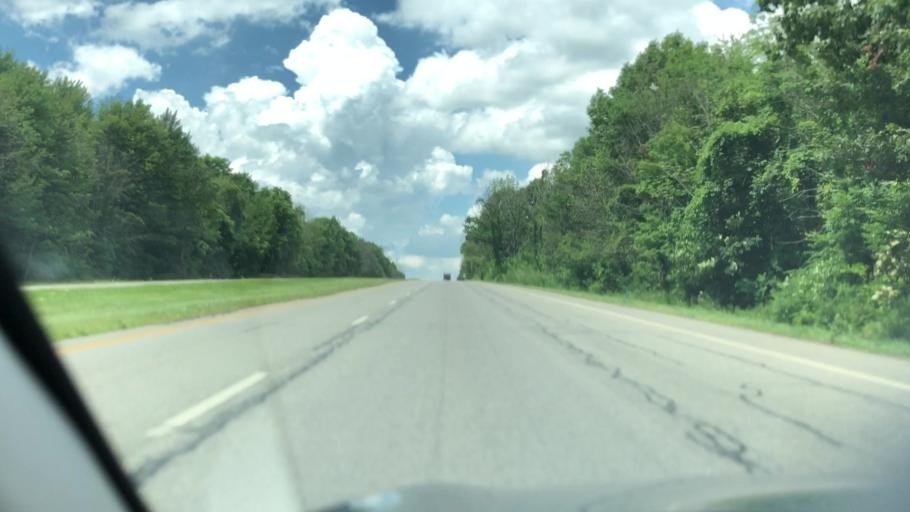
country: US
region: Ohio
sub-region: Stark County
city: Canal Fulton
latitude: 40.8802
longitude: -81.6091
